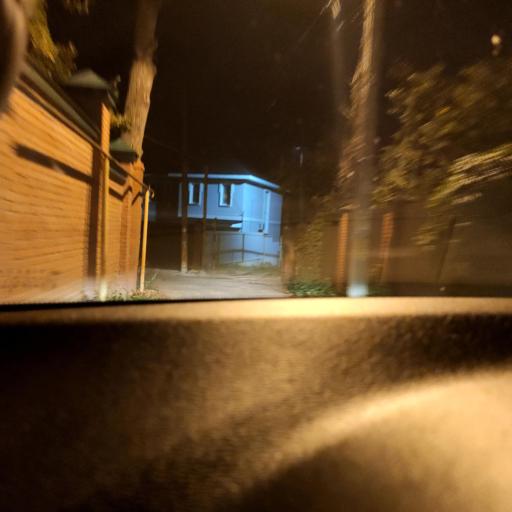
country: RU
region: Samara
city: Samara
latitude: 53.2630
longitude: 50.1964
